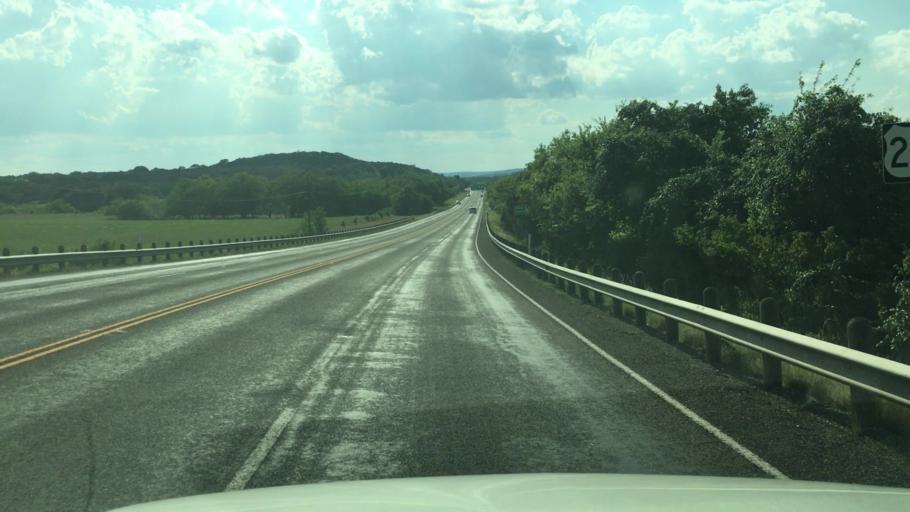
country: US
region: Texas
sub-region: Blanco County
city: Johnson City
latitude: 30.1995
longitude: -98.3615
